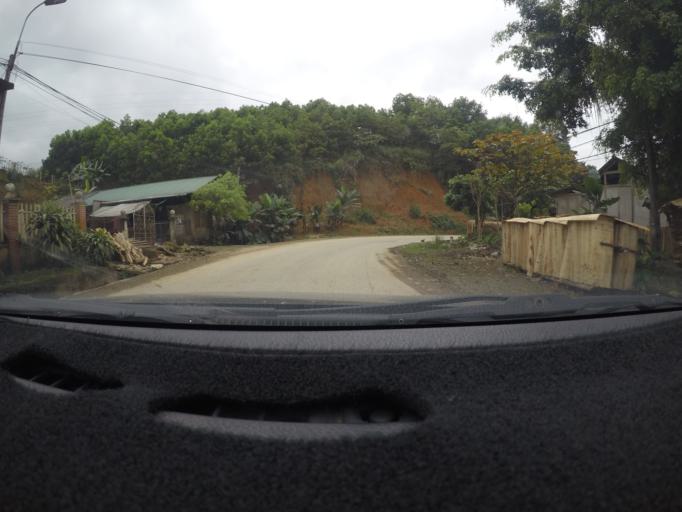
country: VN
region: Yen Bai
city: Co Phuc
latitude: 21.9156
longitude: 104.8091
